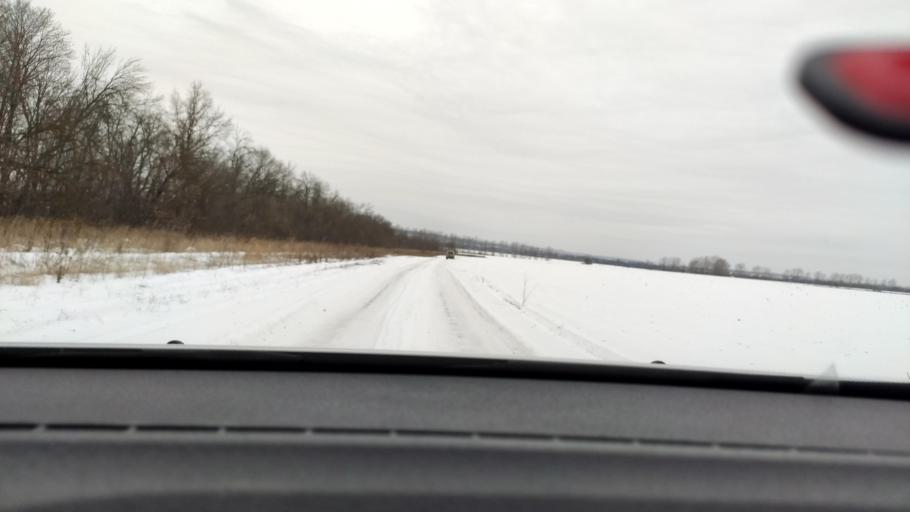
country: RU
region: Voronezj
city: Semiluki
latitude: 51.7164
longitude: 38.9867
